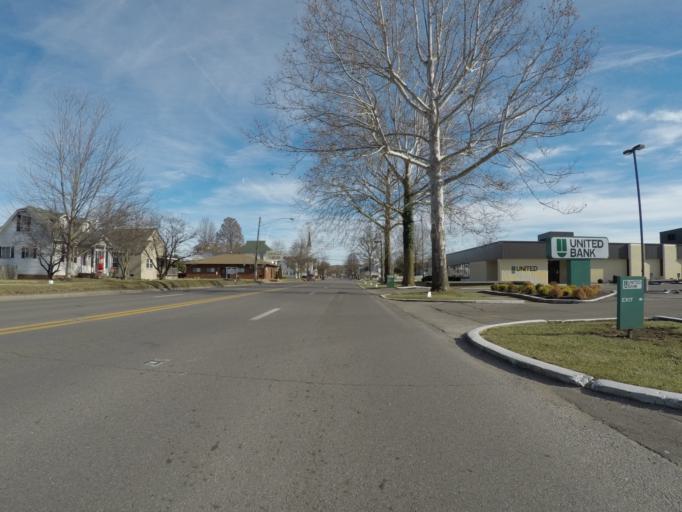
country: US
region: West Virginia
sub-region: Wayne County
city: Ceredo
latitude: 38.3968
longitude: -82.5614
